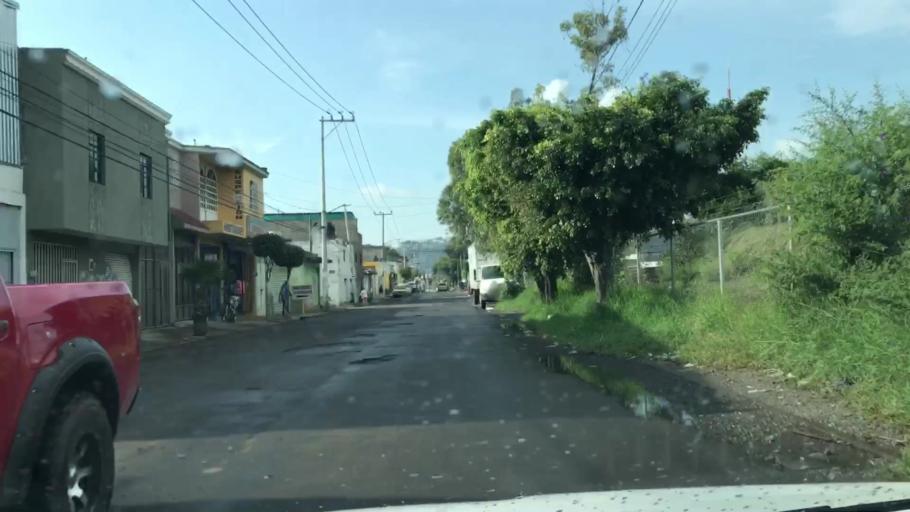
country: MX
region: Jalisco
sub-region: Tlajomulco de Zuniga
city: Palomar
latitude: 20.6314
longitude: -103.4548
